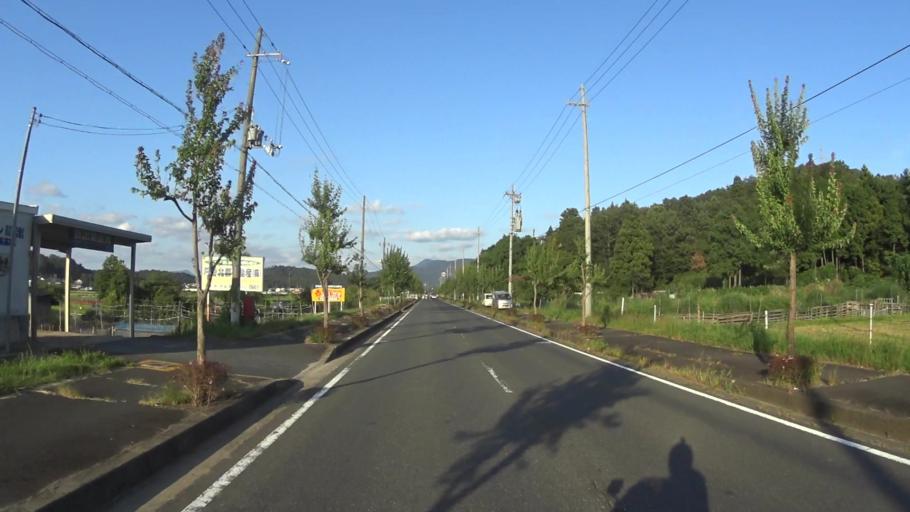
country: JP
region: Kyoto
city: Miyazu
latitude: 35.6033
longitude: 135.0502
